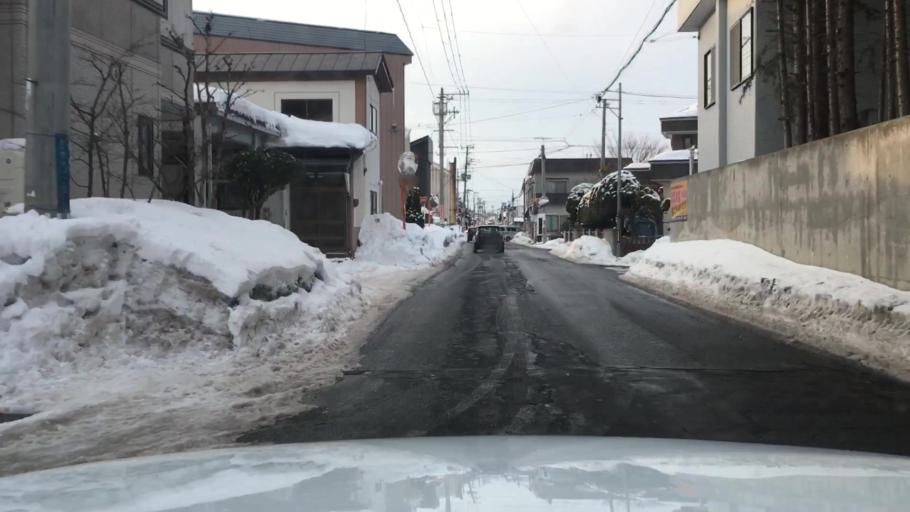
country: JP
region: Aomori
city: Hirosaki
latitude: 40.5826
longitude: 140.4866
